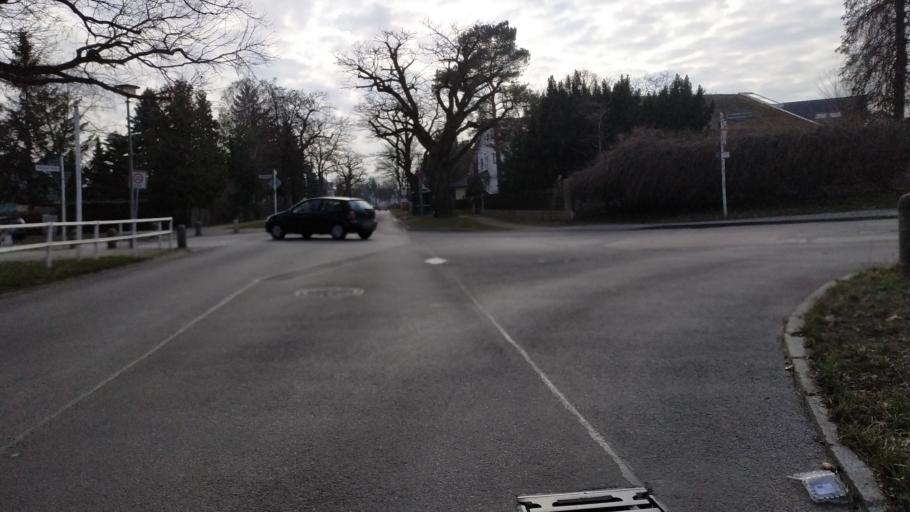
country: DE
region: Berlin
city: Mahlsdorf
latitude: 52.5182
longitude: 13.6075
